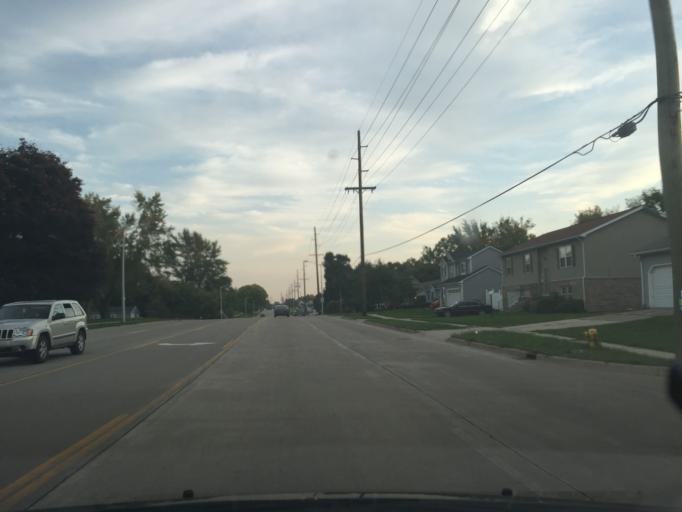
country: US
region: Michigan
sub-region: Oakland County
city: Pontiac
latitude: 42.6330
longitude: -83.2689
